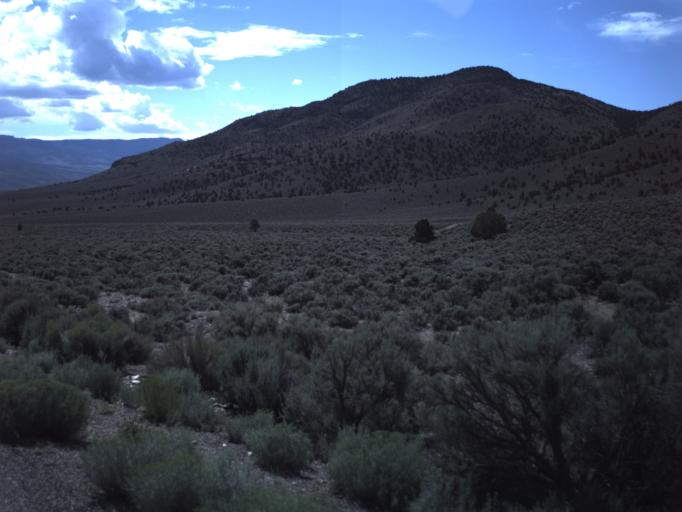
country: US
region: Utah
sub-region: Piute County
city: Junction
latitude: 38.2608
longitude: -112.2491
